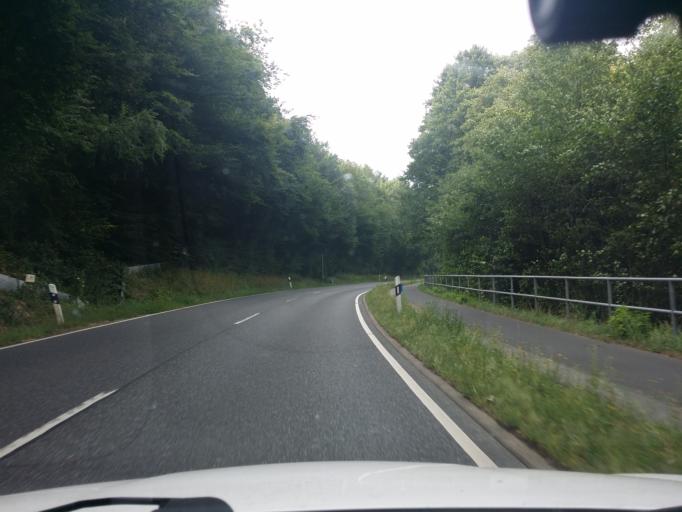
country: DE
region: Hesse
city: Eppstein
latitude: 50.1607
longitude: 8.3780
